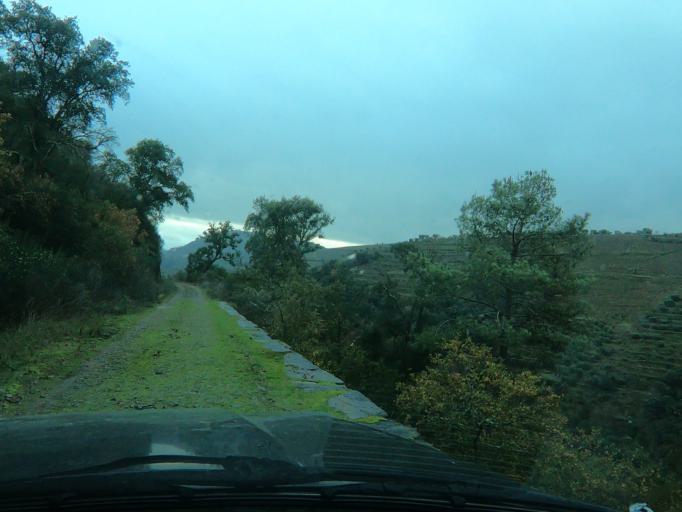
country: PT
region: Vila Real
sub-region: Santa Marta de Penaguiao
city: Santa Marta de Penaguiao
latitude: 41.2112
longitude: -7.7611
